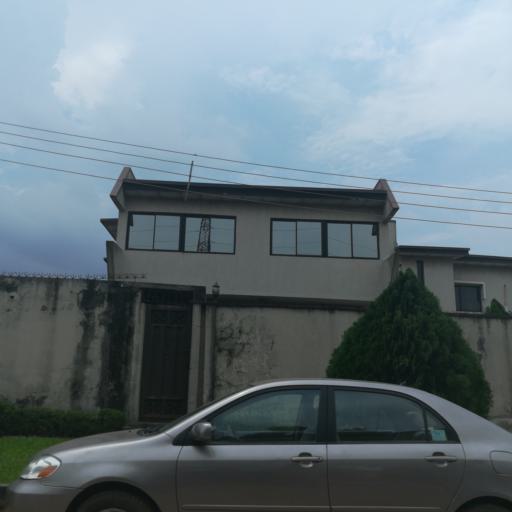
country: NG
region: Lagos
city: Ojota
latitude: 6.5753
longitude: 3.3866
